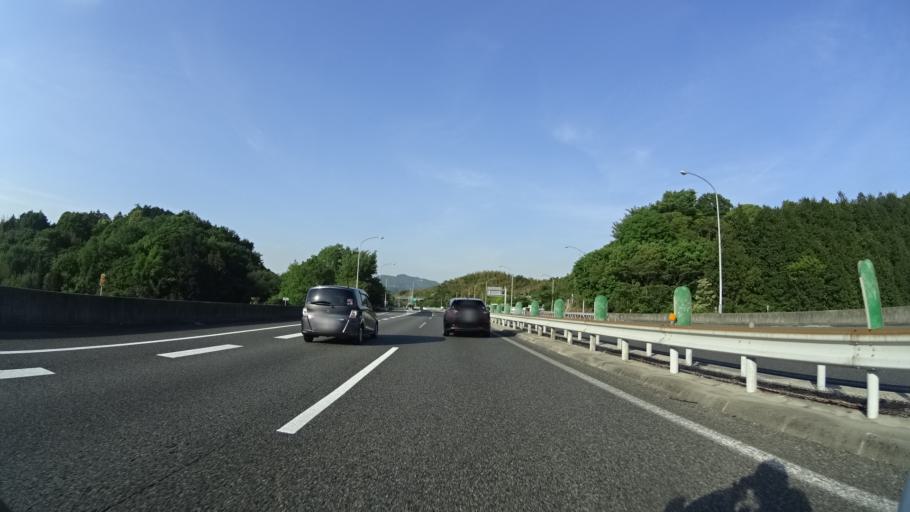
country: JP
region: Ehime
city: Kawanoecho
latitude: 33.9827
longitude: 133.5851
